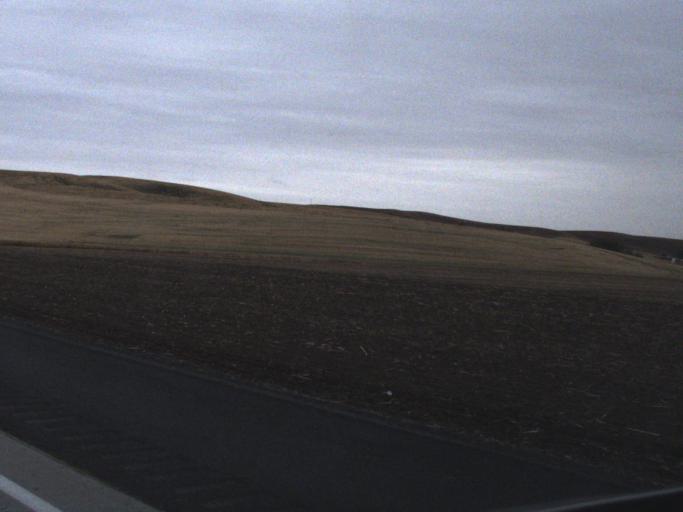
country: US
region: Washington
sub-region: Whitman County
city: Colfax
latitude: 46.9933
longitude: -117.3533
